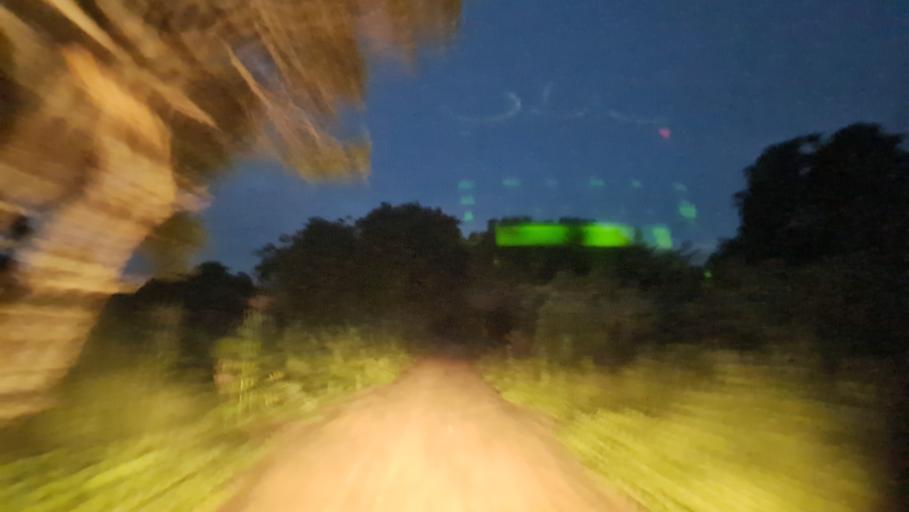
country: MZ
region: Nampula
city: Nampula
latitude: -14.6711
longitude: 39.8343
